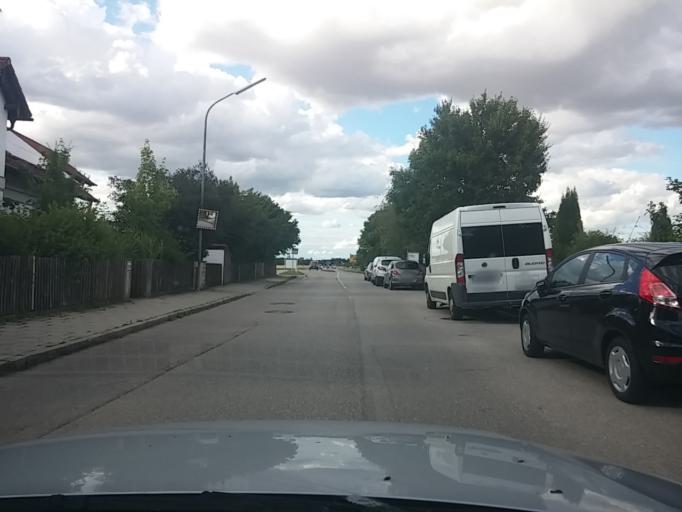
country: DE
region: Bavaria
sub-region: Upper Bavaria
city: Putzbrunn
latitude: 48.0791
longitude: 11.7163
